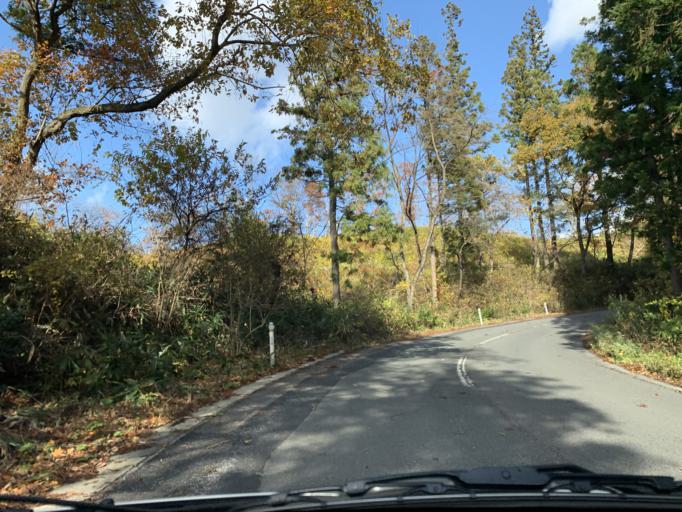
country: JP
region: Iwate
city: Mizusawa
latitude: 39.0429
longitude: 141.0738
